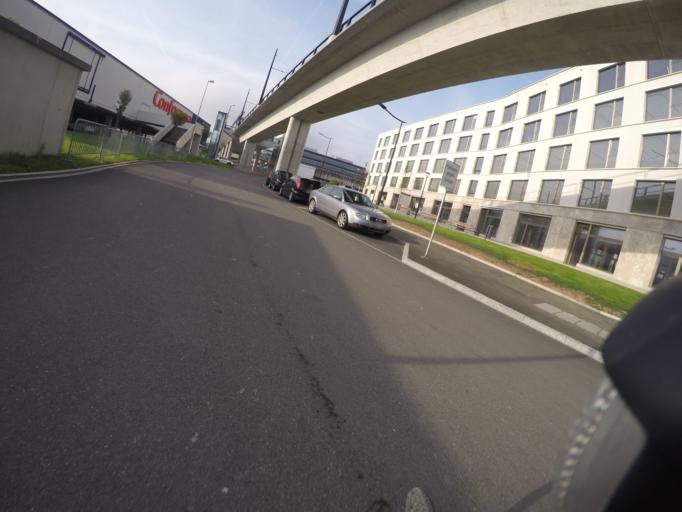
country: CH
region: Zurich
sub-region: Bezirk Buelach
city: Wallisellen / Wallisellen-Ost
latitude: 47.4103
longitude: 8.5981
